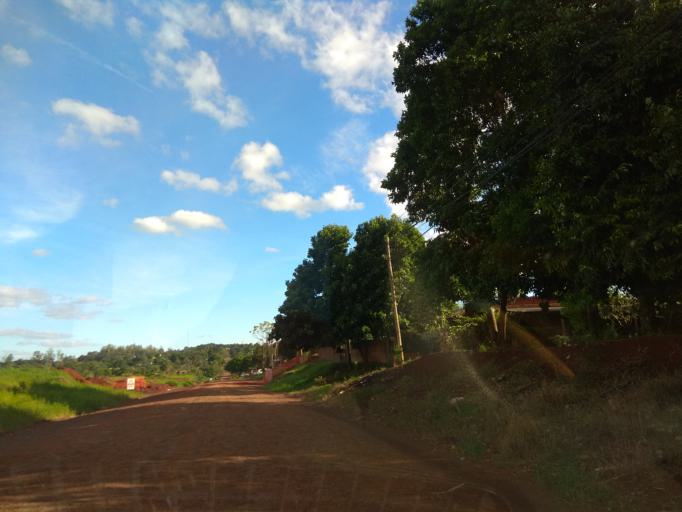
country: AR
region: Misiones
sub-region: Departamento de Capital
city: Posadas
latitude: -27.3916
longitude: -55.9275
